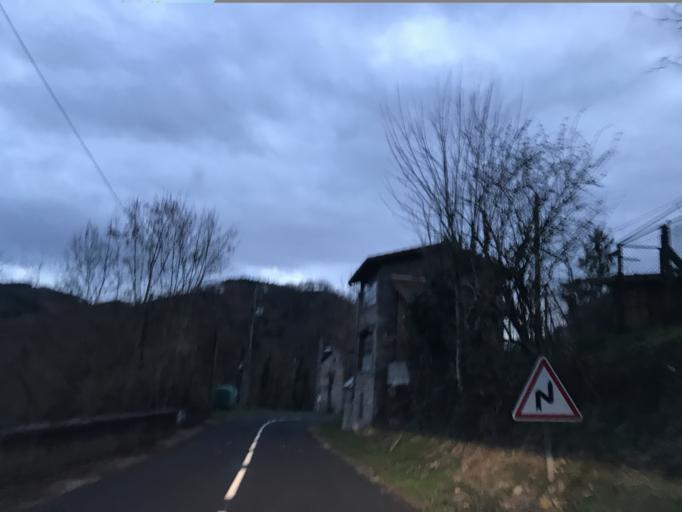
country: FR
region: Auvergne
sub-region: Departement du Puy-de-Dome
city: Thiers
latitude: 45.8674
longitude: 3.5661
